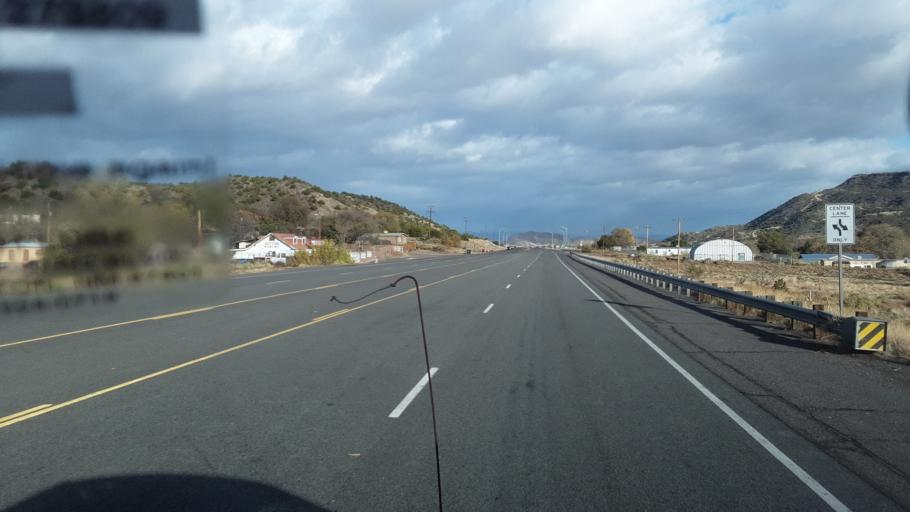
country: US
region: New Mexico
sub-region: Rio Arriba County
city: Ohkay Owingeh
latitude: 36.0681
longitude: -106.1226
